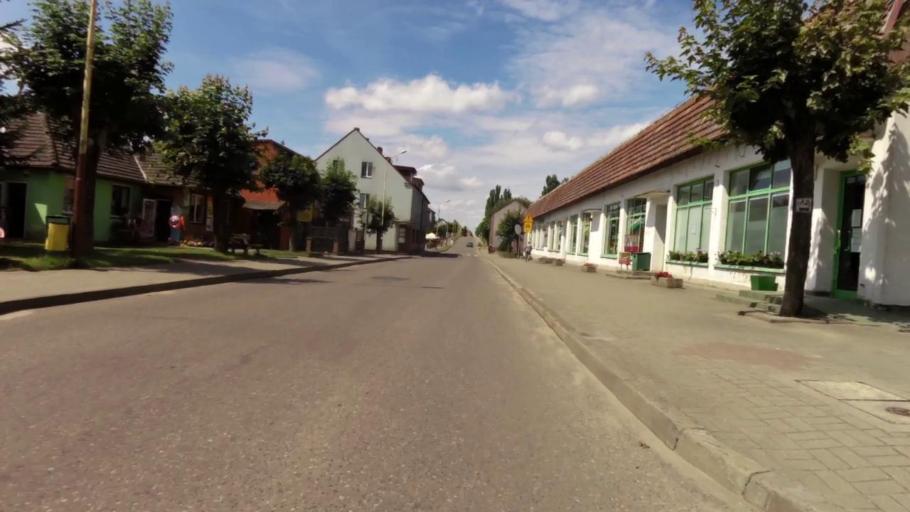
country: PL
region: West Pomeranian Voivodeship
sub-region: Powiat stargardzki
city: Insko
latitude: 53.4362
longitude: 15.5494
